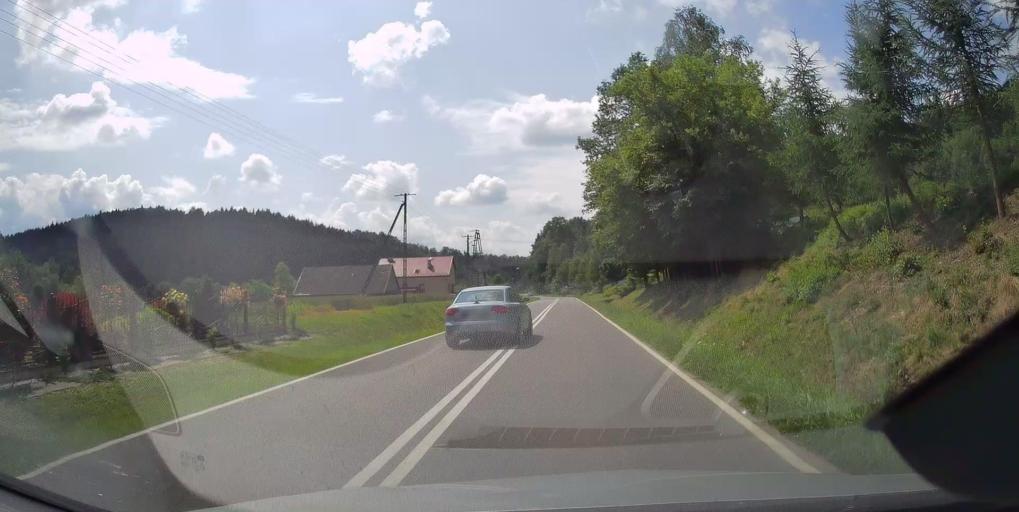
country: PL
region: Lesser Poland Voivodeship
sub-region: Powiat tarnowski
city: Zakliczyn
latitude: 49.8075
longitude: 20.7971
